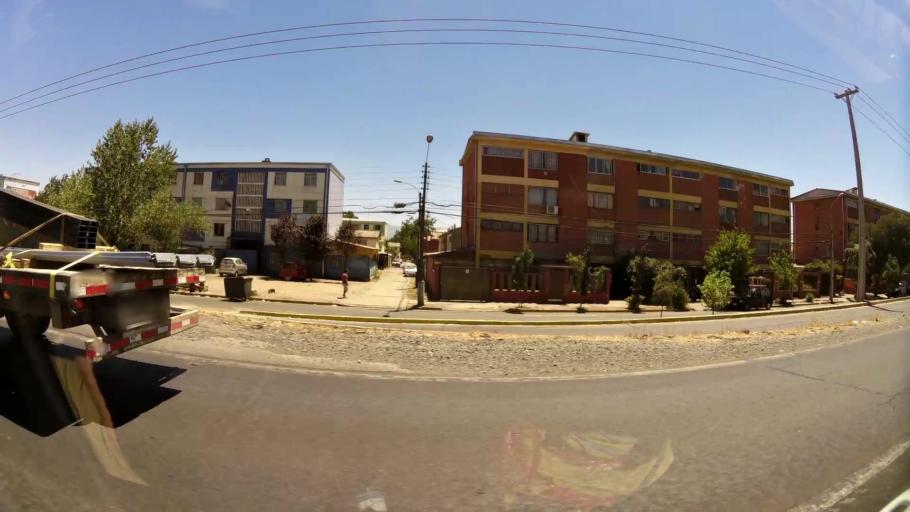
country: CL
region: O'Higgins
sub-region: Provincia de Cachapoal
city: Rancagua
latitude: -34.1829
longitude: -70.7386
